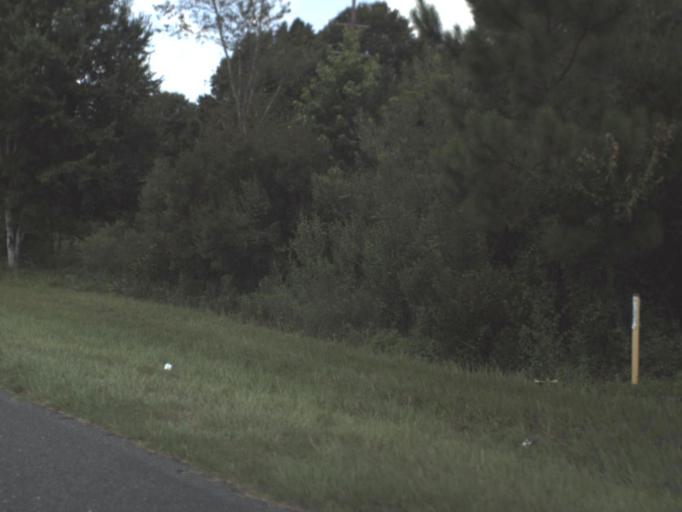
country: US
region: Florida
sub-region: Union County
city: Lake Butler
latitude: 29.9953
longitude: -82.3779
